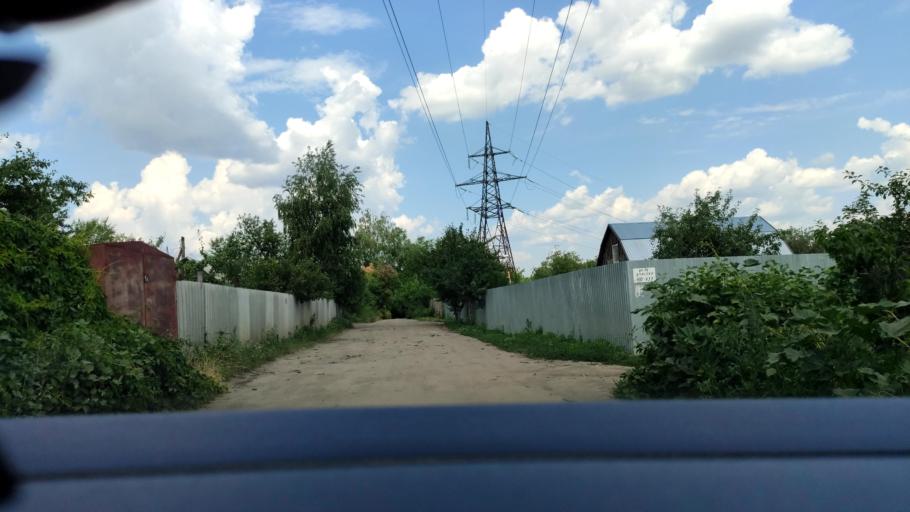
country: RU
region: Voronezj
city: Maslovka
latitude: 51.6053
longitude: 39.2860
